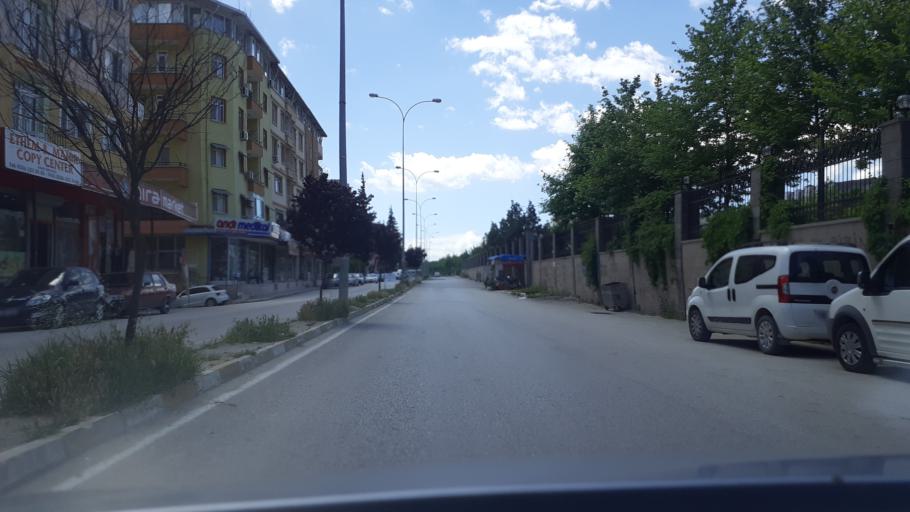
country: TR
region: Hatay
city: Anayazi
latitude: 36.3381
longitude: 36.2004
